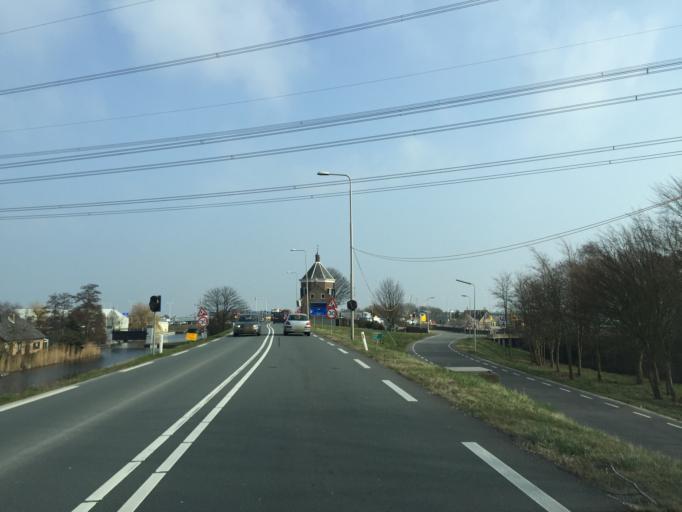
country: NL
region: South Holland
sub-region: Gemeente Westland
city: Maasdijk
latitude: 51.9714
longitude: 4.2011
